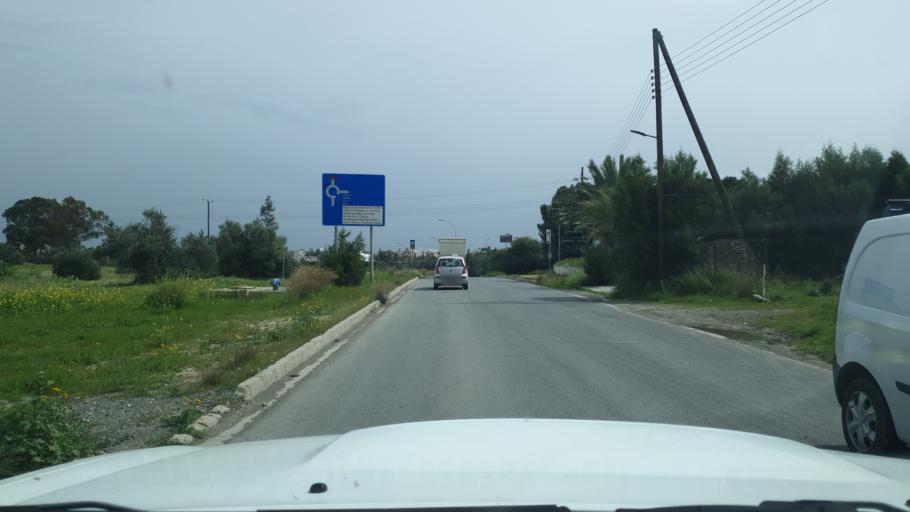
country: CY
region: Lefkosia
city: Tseri
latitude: 35.1050
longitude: 33.3652
